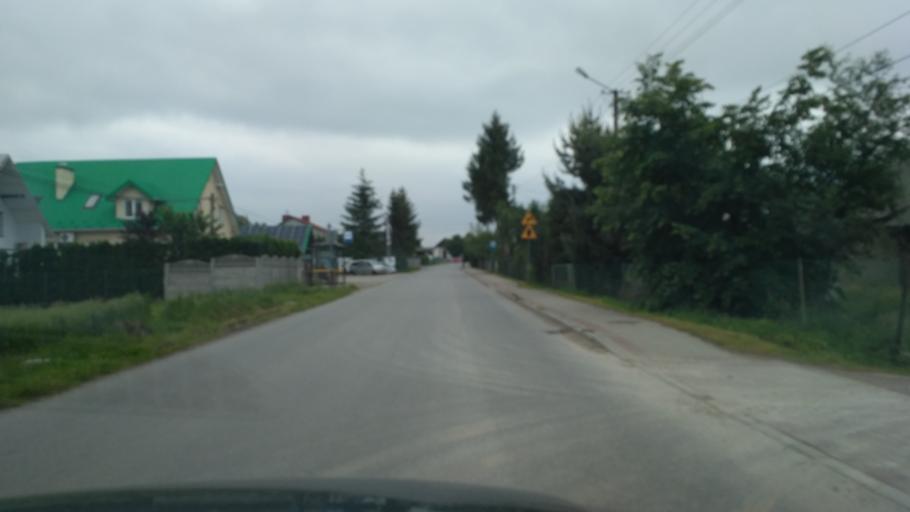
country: PL
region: Subcarpathian Voivodeship
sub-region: Powiat ropczycko-sedziszowski
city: Sedziszow Malopolski
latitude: 50.0974
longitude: 21.6650
